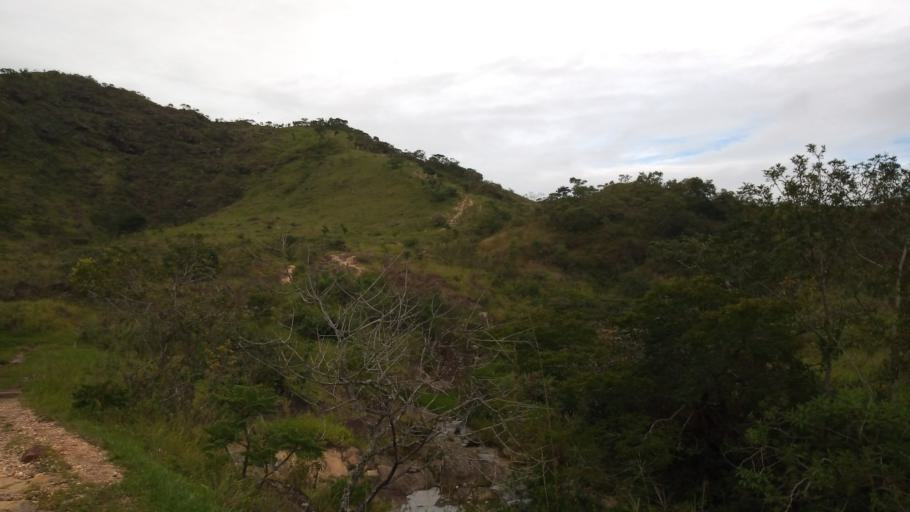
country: BR
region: Minas Gerais
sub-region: Sao Joao Del Rei
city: Sao Joao del Rei
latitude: -21.1261
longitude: -44.2715
